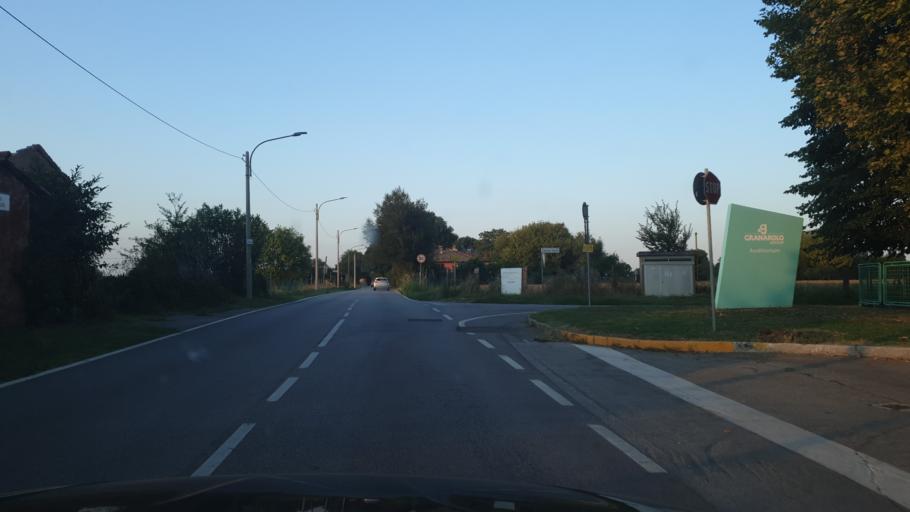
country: IT
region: Emilia-Romagna
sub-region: Provincia di Bologna
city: Quarto Inferiore
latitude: 44.5333
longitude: 11.3888
